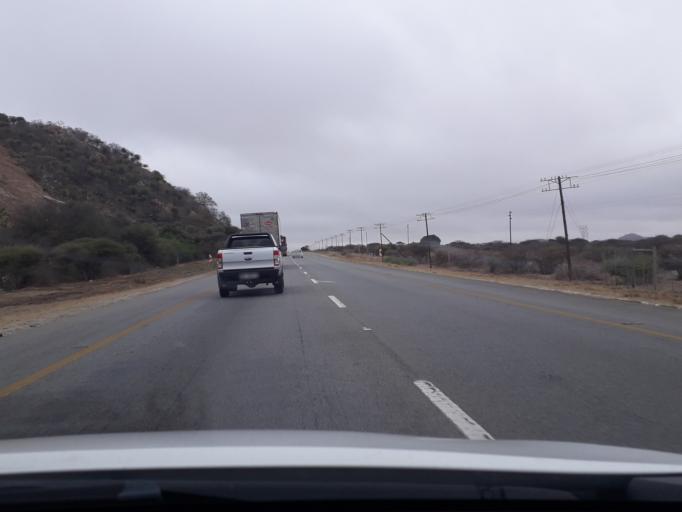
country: ZA
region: Limpopo
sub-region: Capricorn District Municipality
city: Mankoeng
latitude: -23.5269
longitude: 29.7054
